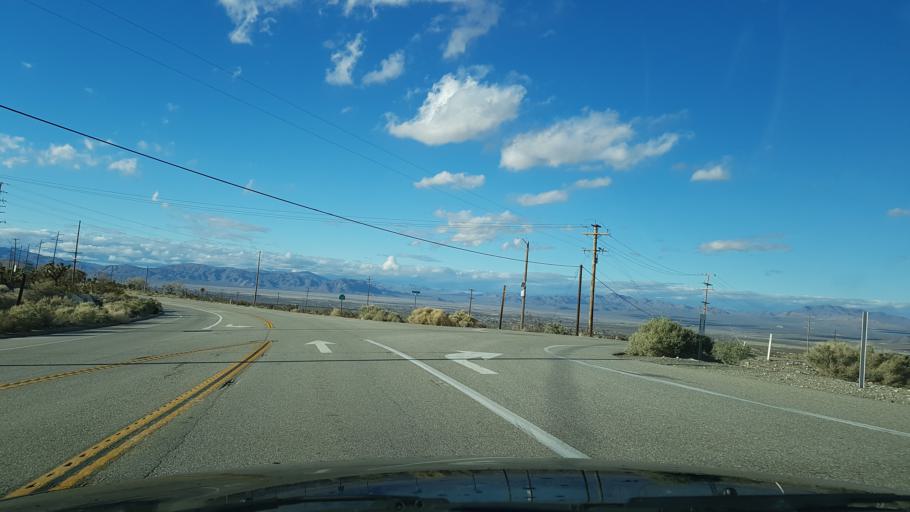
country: US
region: California
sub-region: San Bernardino County
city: Big Bear City
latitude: 34.3726
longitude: -116.8598
